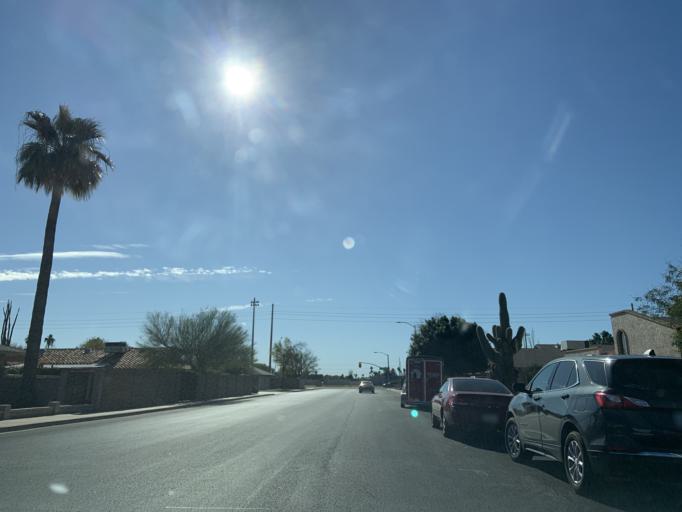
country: US
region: Arizona
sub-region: Maricopa County
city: San Carlos
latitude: 33.3654
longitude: -111.8642
